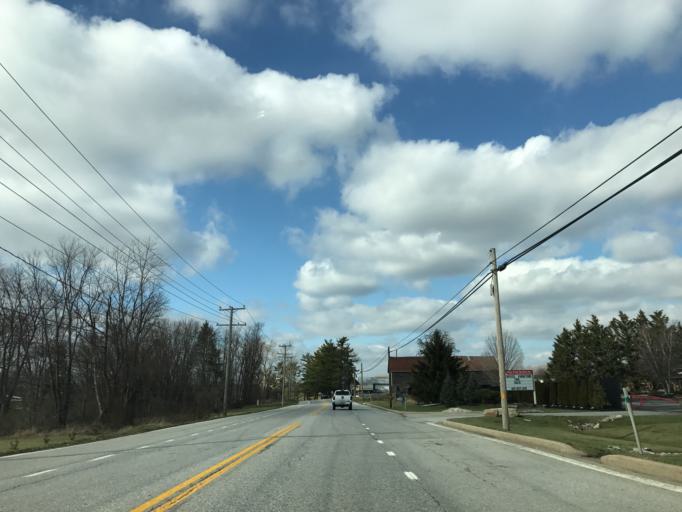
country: US
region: Maryland
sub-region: Carroll County
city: Westminster
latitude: 39.6212
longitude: -76.9970
